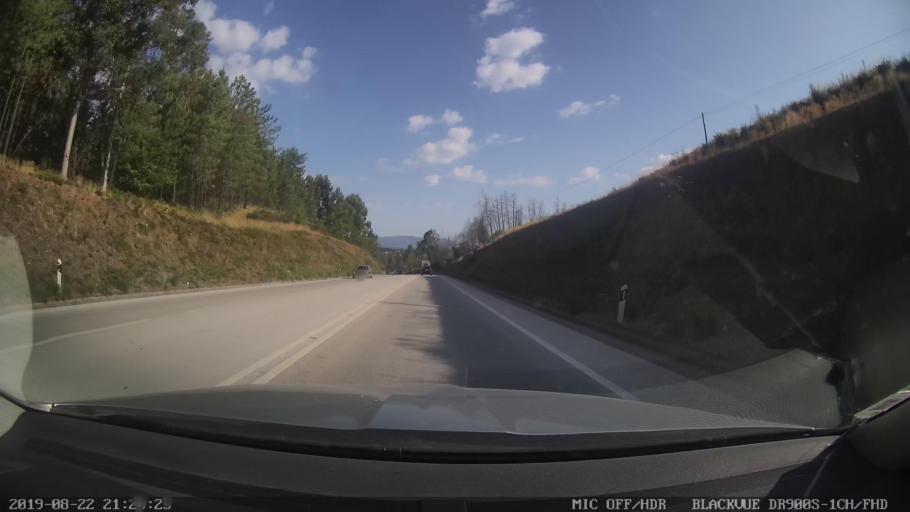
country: PT
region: Leiria
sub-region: Pedrogao Grande
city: Pedrogao Grande
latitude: 39.8918
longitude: -8.1211
